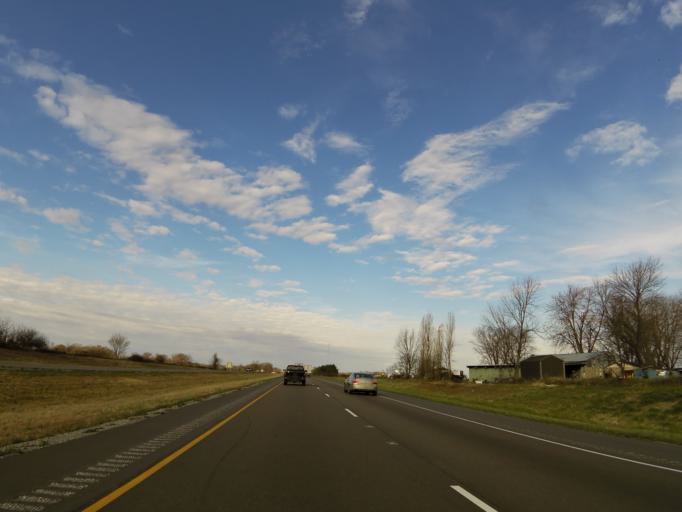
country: US
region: Illinois
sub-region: Washington County
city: Okawville
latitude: 38.4487
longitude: -89.5468
